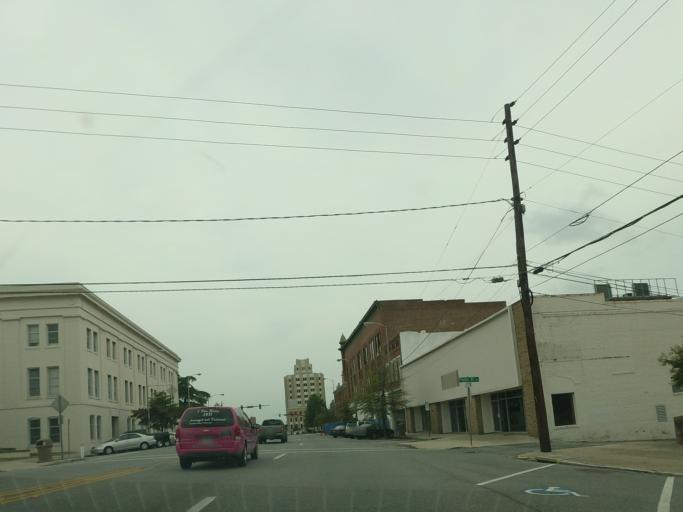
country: US
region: Georgia
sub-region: Bibb County
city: Macon
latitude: 32.8355
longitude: -83.6323
